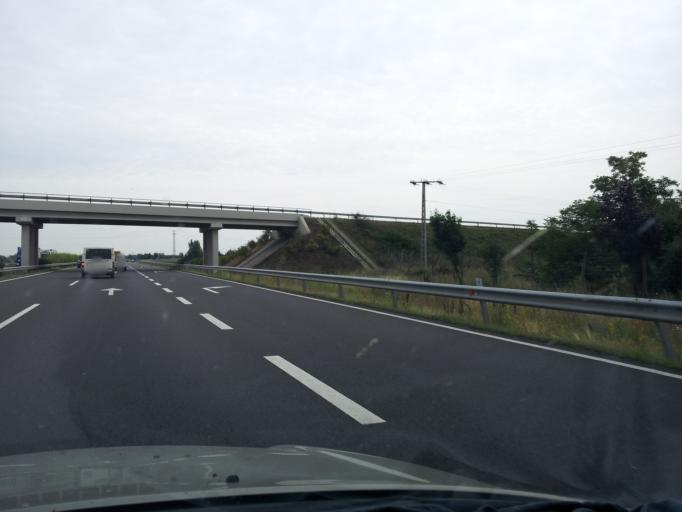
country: HU
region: Heves
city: Karacsond
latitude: 47.7065
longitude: 20.0995
